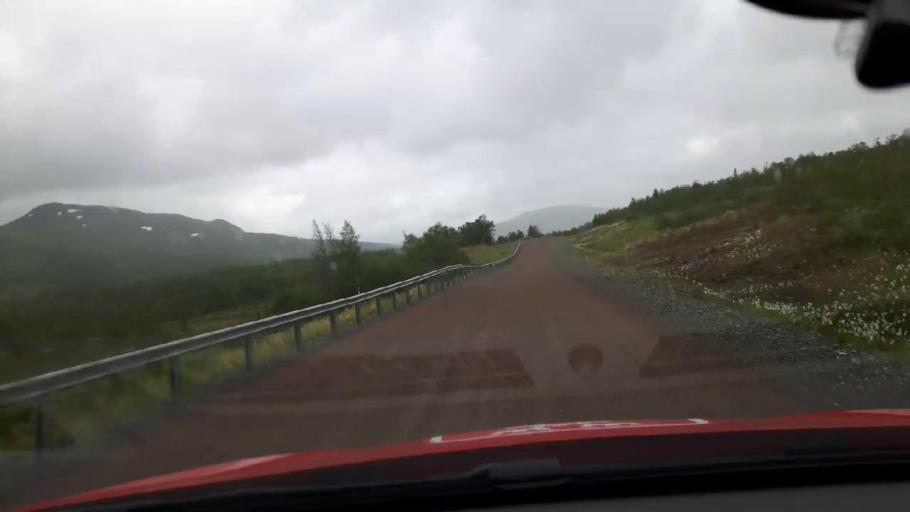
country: NO
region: Nord-Trondelag
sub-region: Meraker
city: Meraker
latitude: 63.1961
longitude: 12.3893
